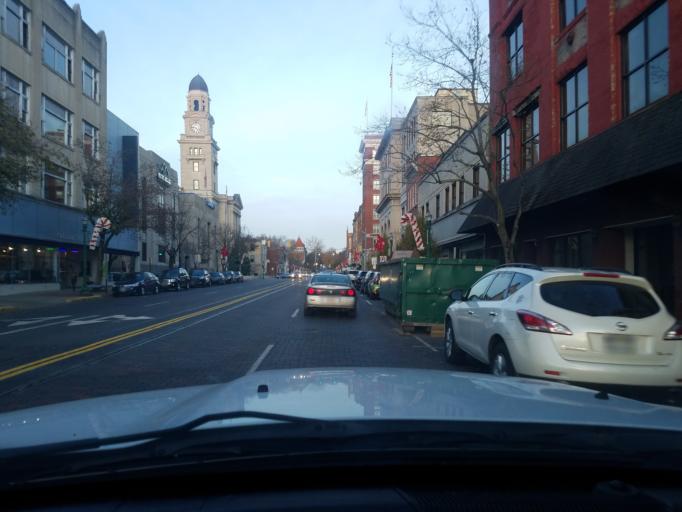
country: US
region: Ohio
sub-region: Washington County
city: Marietta
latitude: 39.4148
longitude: -81.4555
